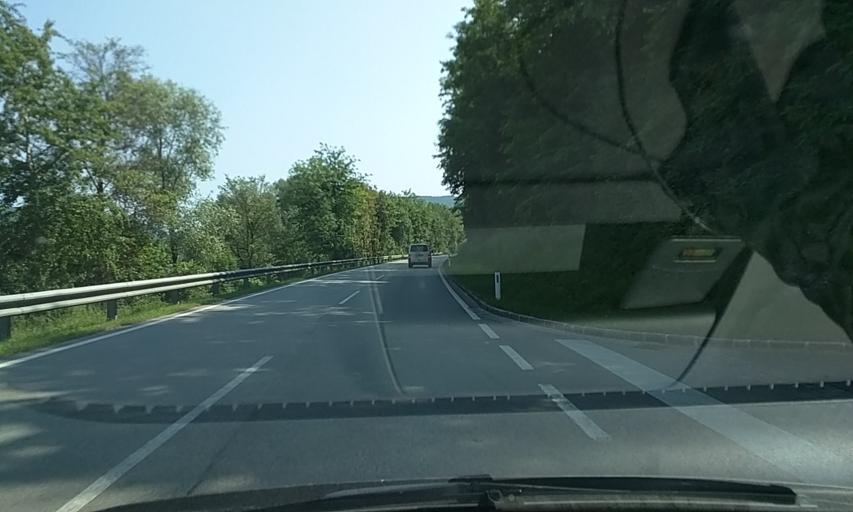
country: AT
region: Lower Austria
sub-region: Politischer Bezirk Melk
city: Emmersdorf an der Donau
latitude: 48.2459
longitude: 15.3556
